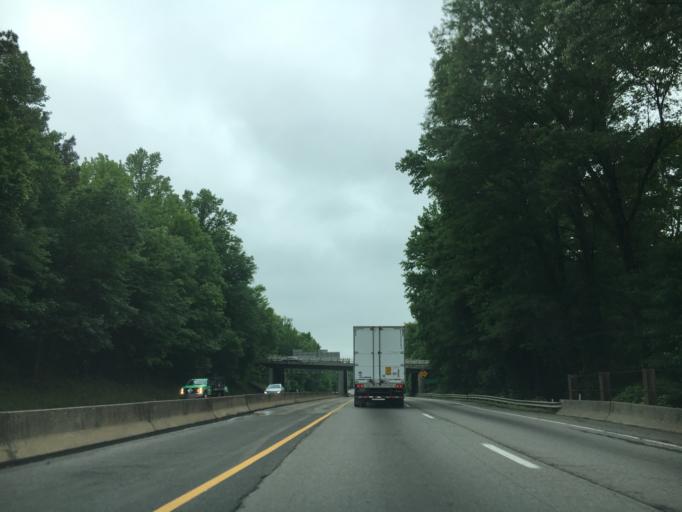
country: US
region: Virginia
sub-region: City of Petersburg
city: Petersburg
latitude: 37.2141
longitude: -77.3968
